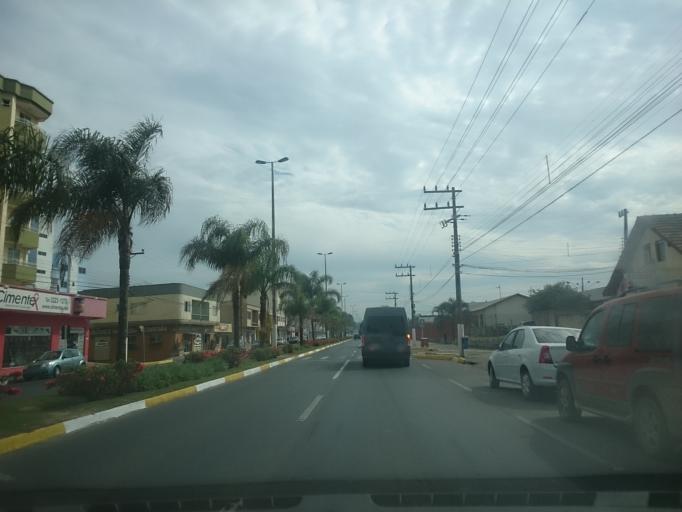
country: BR
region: Santa Catarina
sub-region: Lages
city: Lages
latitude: -27.8007
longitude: -50.3052
